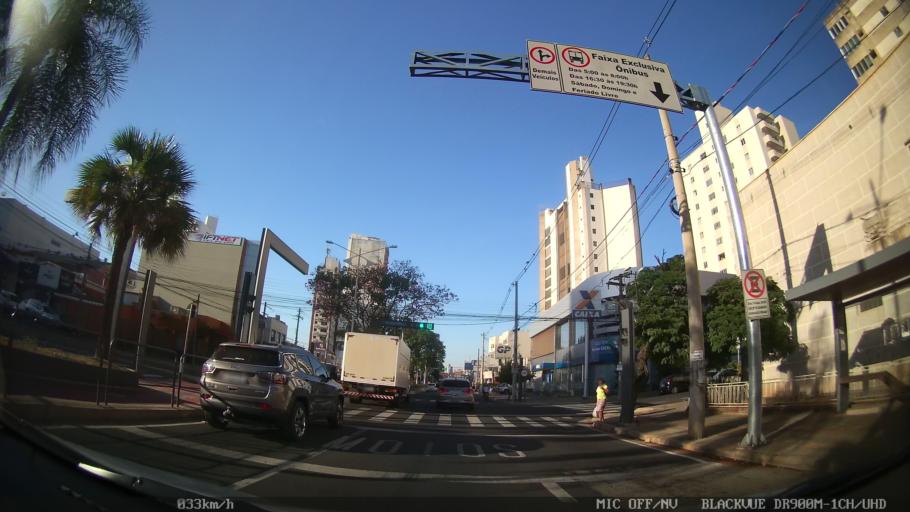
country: BR
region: Sao Paulo
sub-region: Sao Jose Do Rio Preto
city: Sao Jose do Rio Preto
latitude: -20.8091
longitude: -49.3828
